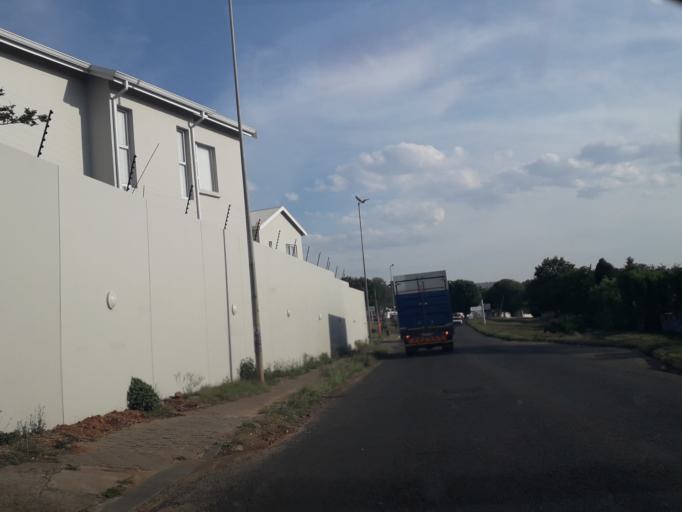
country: ZA
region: Gauteng
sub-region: City of Johannesburg Metropolitan Municipality
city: Johannesburg
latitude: -26.1277
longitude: 27.9885
